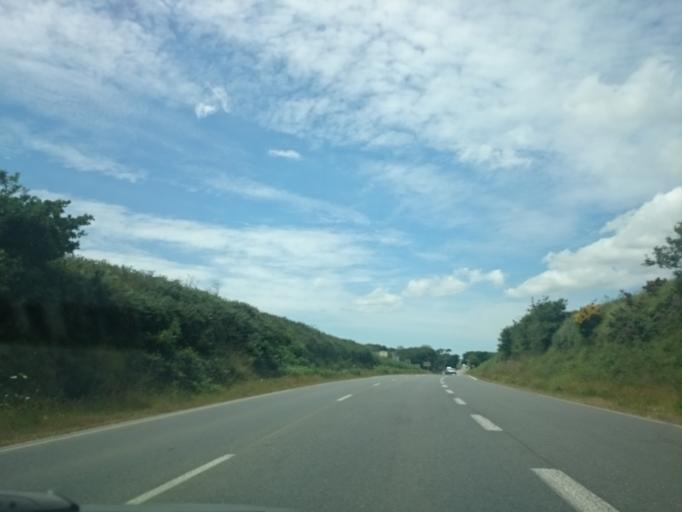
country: FR
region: Brittany
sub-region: Departement du Finistere
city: Plouzane
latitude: 48.3603
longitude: -4.6465
